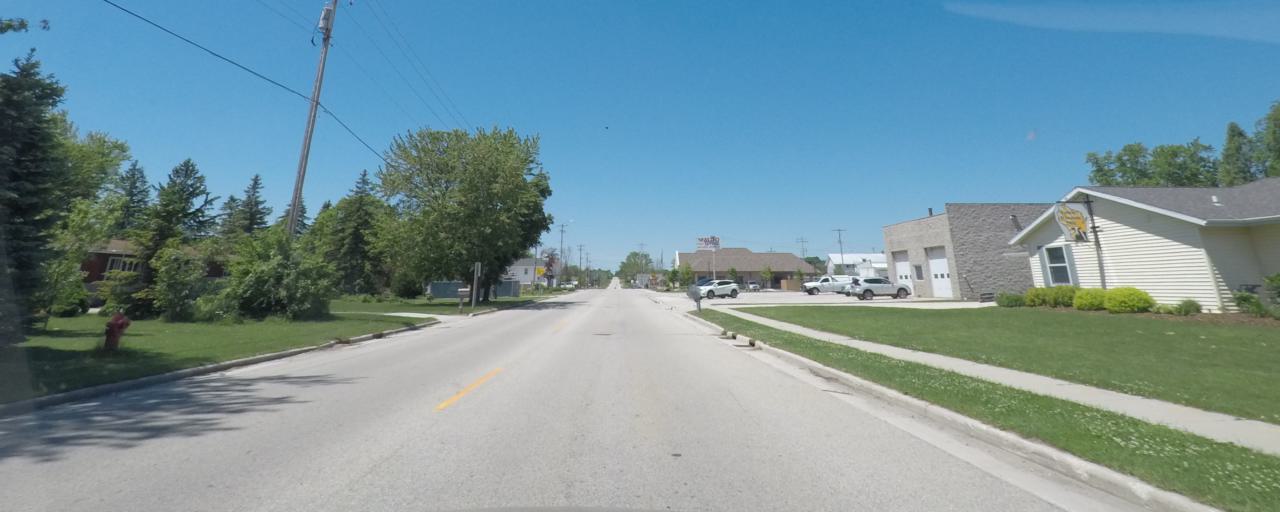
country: US
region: Wisconsin
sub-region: Sheboygan County
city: Plymouth
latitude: 43.6746
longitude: -87.9510
